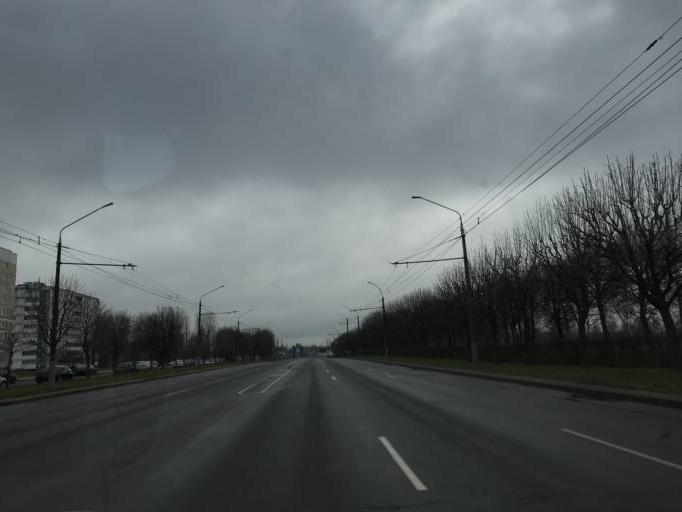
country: BY
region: Mogilev
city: Mahilyow
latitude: 53.8645
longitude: 30.3328
